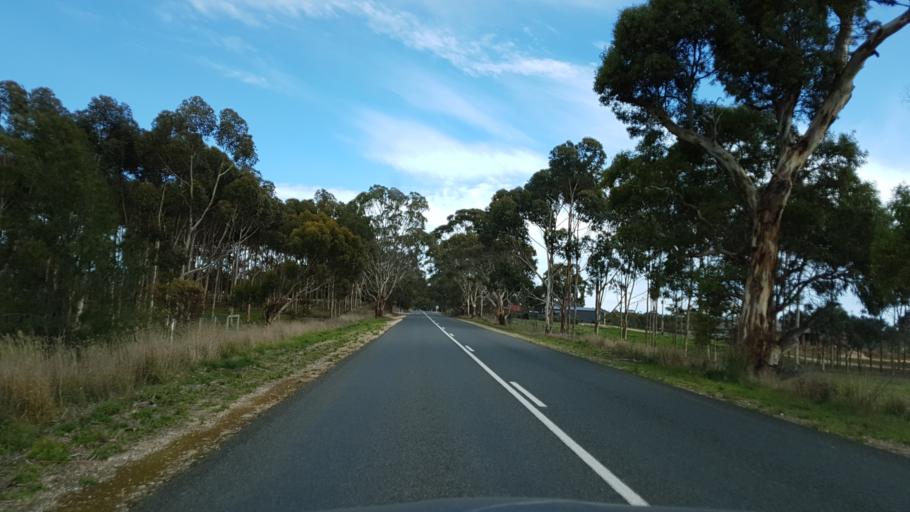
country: AU
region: South Australia
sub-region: Mount Barker
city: Macclesfield
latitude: -35.1477
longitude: 138.9318
